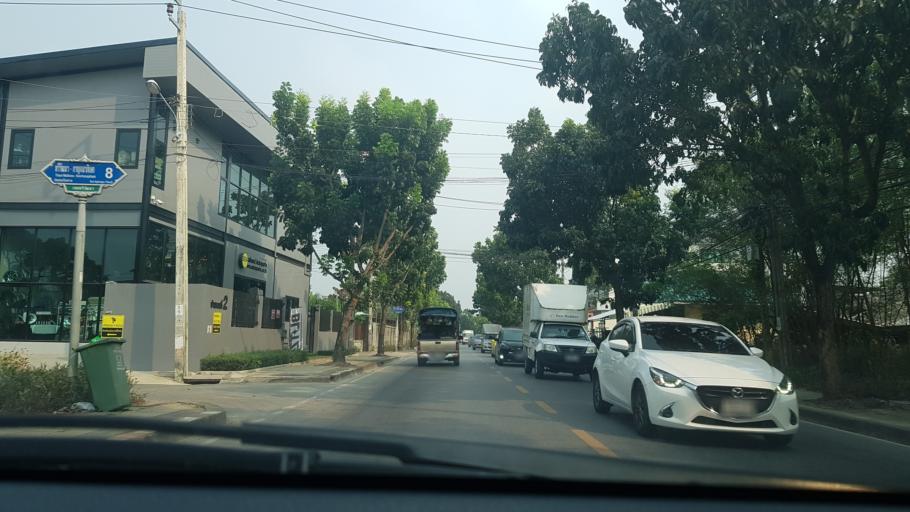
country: TH
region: Bangkok
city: Thawi Watthana
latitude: 13.7574
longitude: 100.3811
